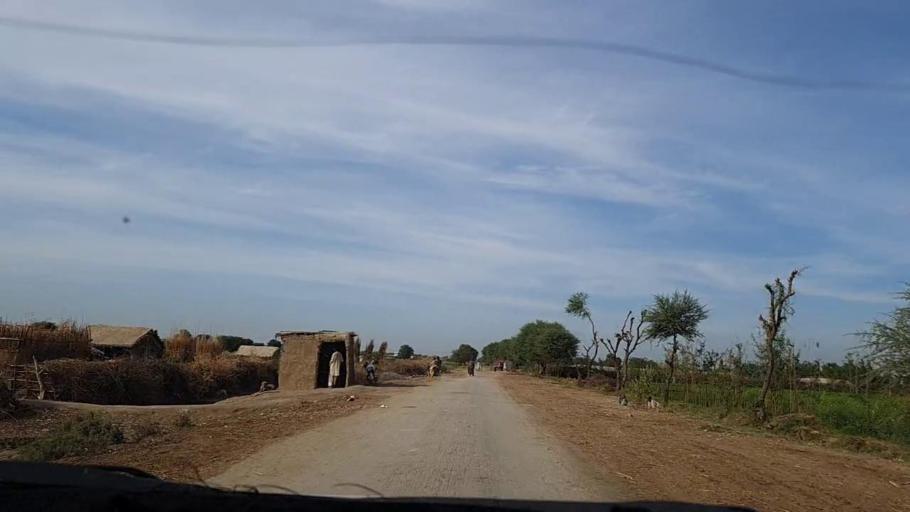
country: PK
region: Sindh
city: Dhoro Naro
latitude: 25.4413
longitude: 69.5122
